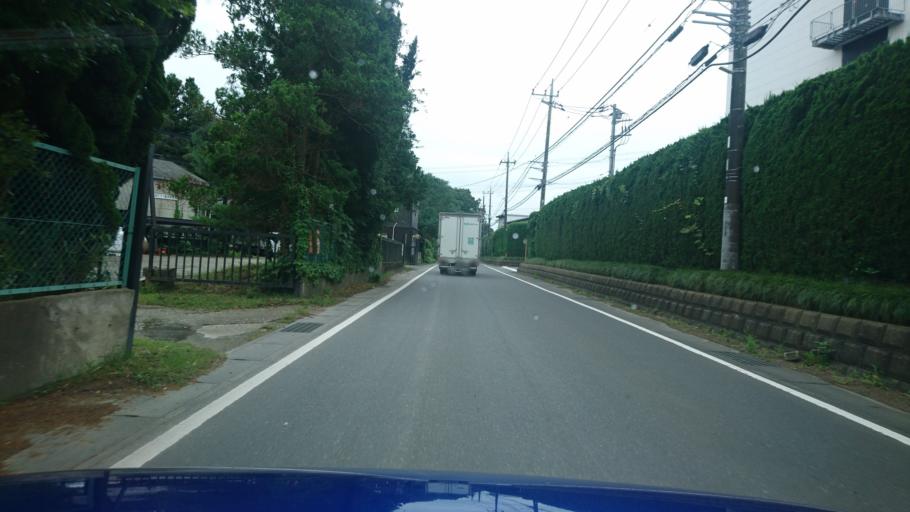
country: JP
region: Ibaraki
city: Ushiku
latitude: 36.0038
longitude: 140.1381
